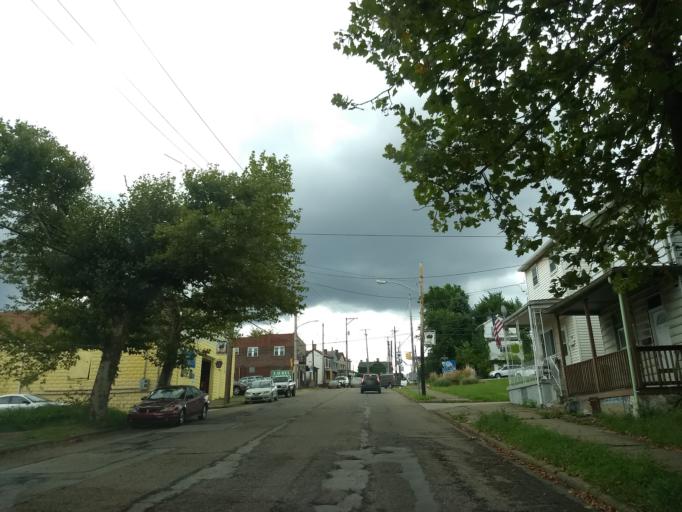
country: US
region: Pennsylvania
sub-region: Allegheny County
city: Homestead
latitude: 40.4024
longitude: -79.9075
